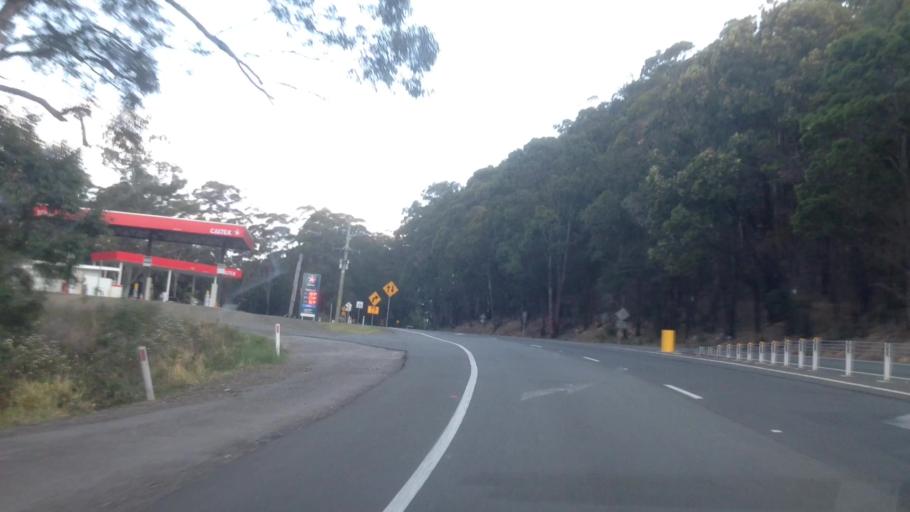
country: AU
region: New South Wales
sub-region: Lake Macquarie Shire
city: Cooranbong
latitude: -32.9635
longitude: 151.4790
